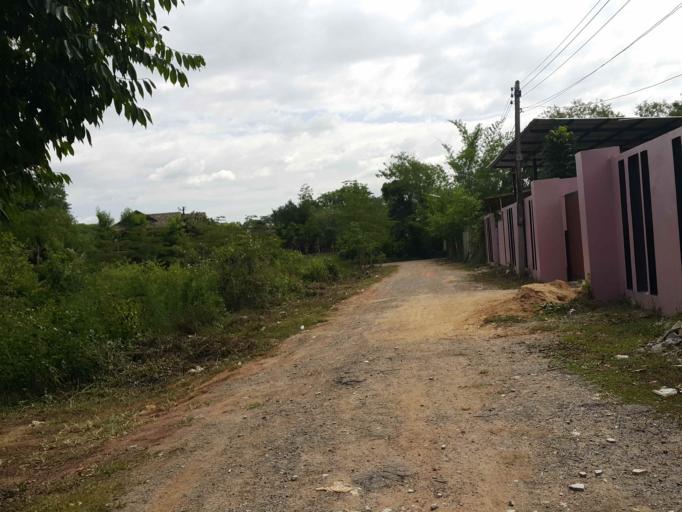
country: TH
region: Chiang Mai
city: San Kamphaeng
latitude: 18.7550
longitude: 99.0930
